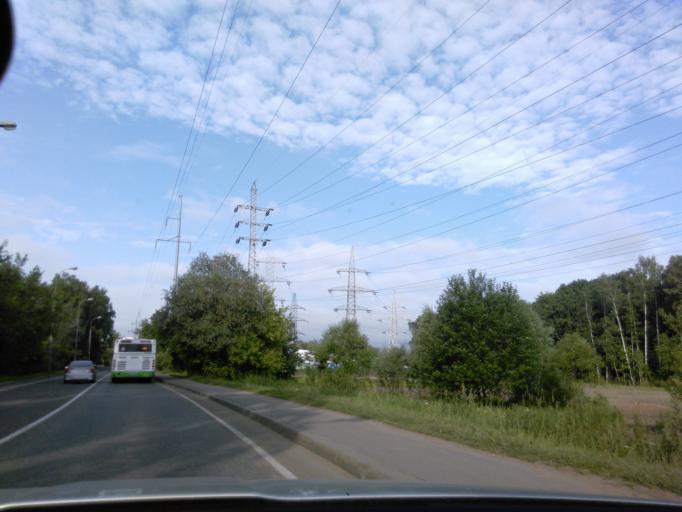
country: RU
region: Moskovskaya
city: Levoberezhnaya
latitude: 55.8798
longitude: 37.4773
